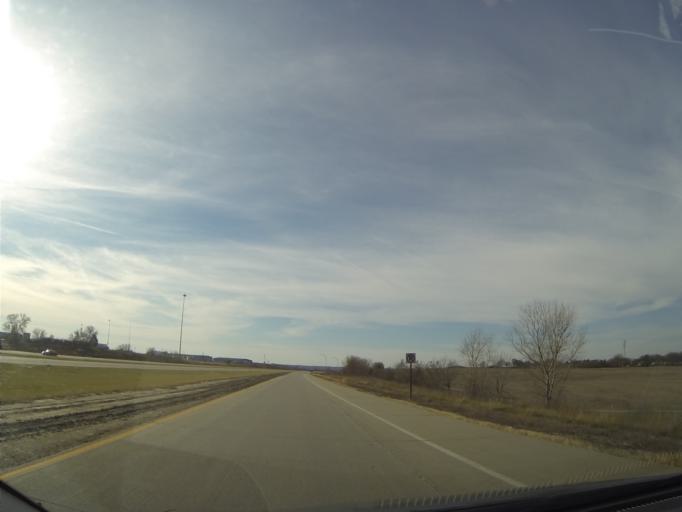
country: US
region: Nebraska
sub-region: Sarpy County
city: Gretna
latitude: 41.0940
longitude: -96.2562
